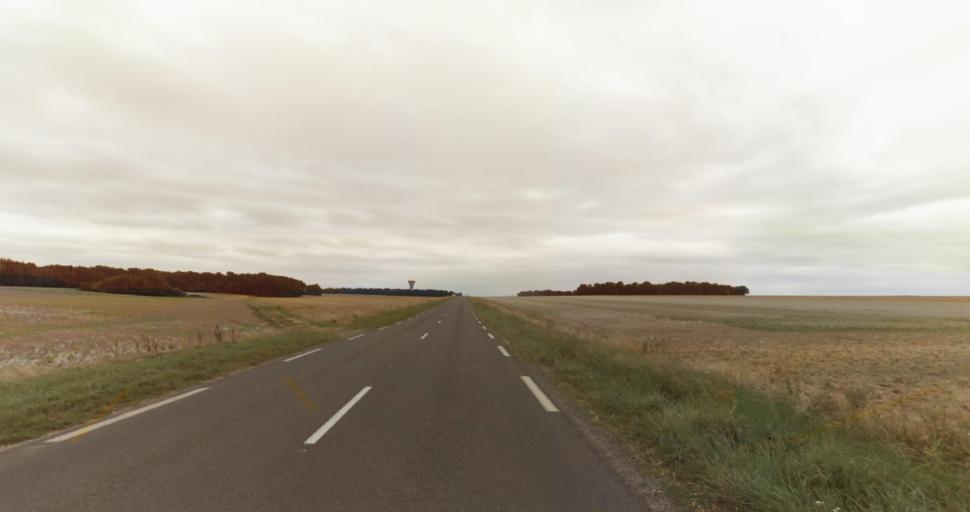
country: FR
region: Haute-Normandie
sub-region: Departement de l'Eure
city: Pacy-sur-Eure
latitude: 48.9438
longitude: 1.3022
